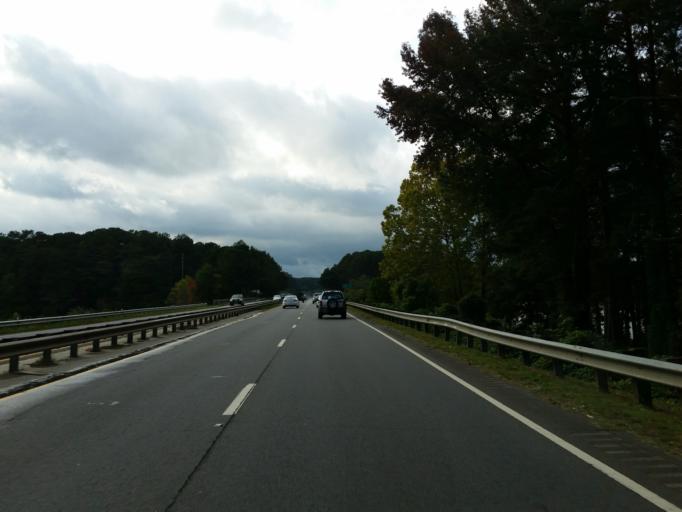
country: US
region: Georgia
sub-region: Cobb County
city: Acworth
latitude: 34.0553
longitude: -84.7078
